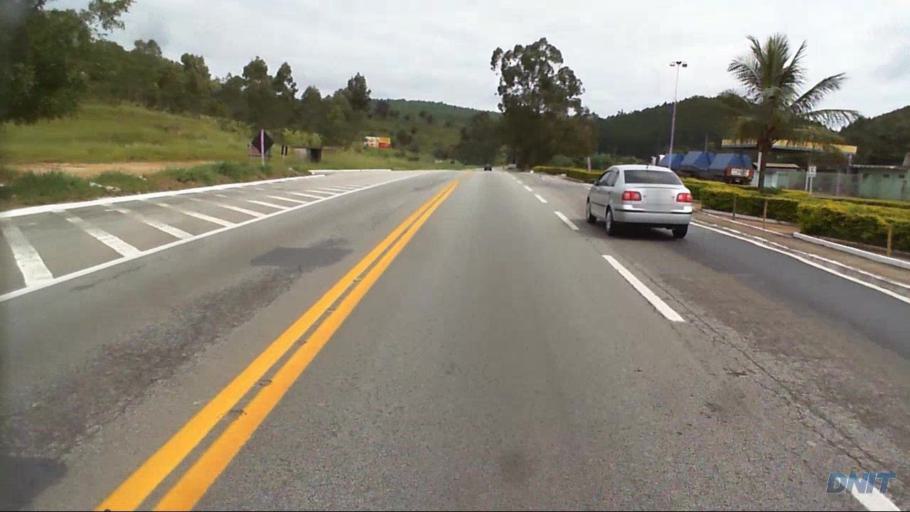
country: BR
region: Minas Gerais
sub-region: Caete
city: Caete
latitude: -19.7246
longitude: -43.5847
